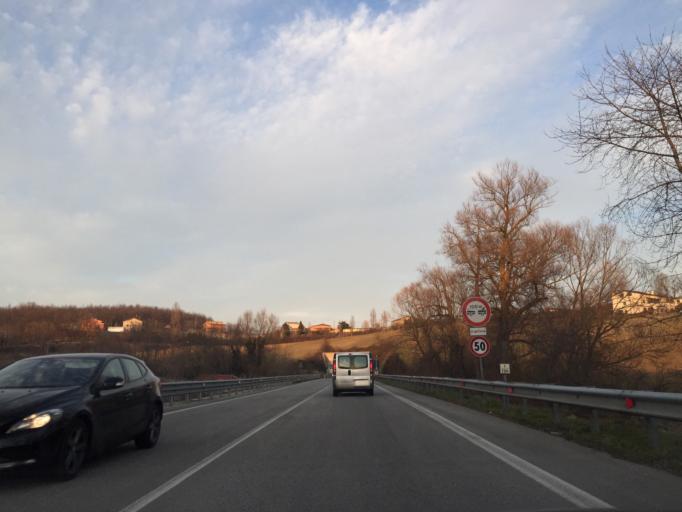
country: IT
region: Molise
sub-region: Provincia di Campobasso
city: Mimosa-Poggio Verde-Nuova Comunita
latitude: 41.5447
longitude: 14.6253
